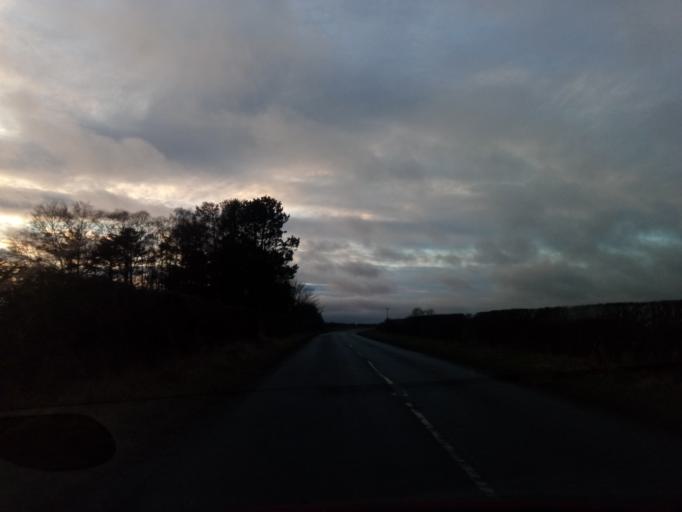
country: GB
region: England
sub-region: Northumberland
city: Morpeth
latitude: 55.1402
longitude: -1.7400
